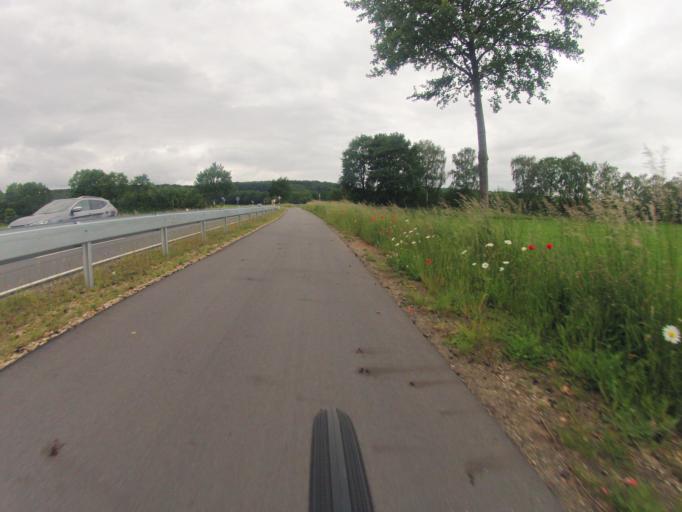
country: DE
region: North Rhine-Westphalia
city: Ibbenburen
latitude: 52.2468
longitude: 7.7586
